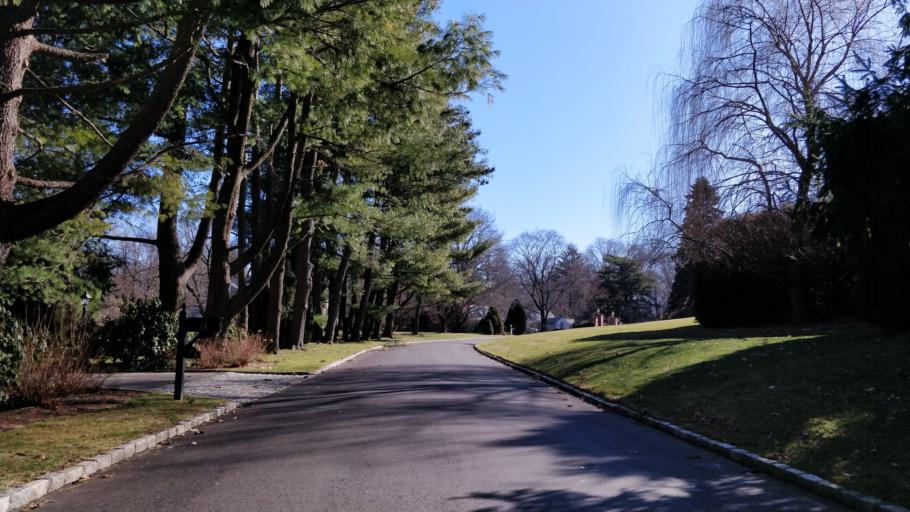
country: US
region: New York
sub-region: Nassau County
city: Brookville
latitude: 40.8146
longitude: -73.5729
